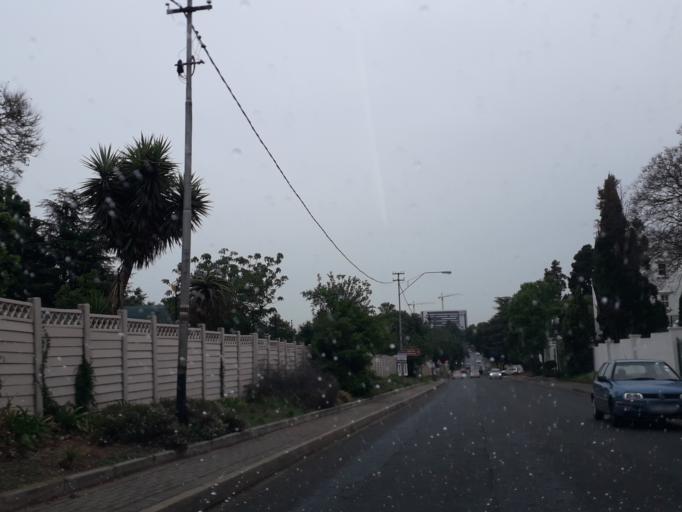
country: ZA
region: Gauteng
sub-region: City of Johannesburg Metropolitan Municipality
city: Johannesburg
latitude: -26.1325
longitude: 28.0451
